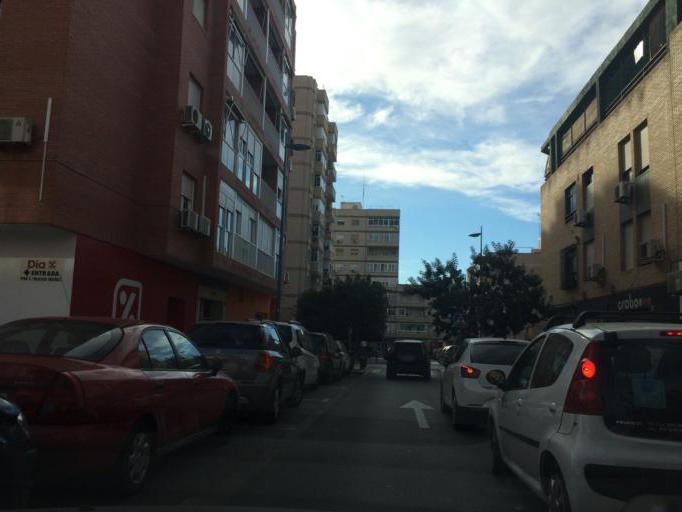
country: ES
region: Andalusia
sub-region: Provincia de Almeria
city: Almeria
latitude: 36.8429
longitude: -2.4492
